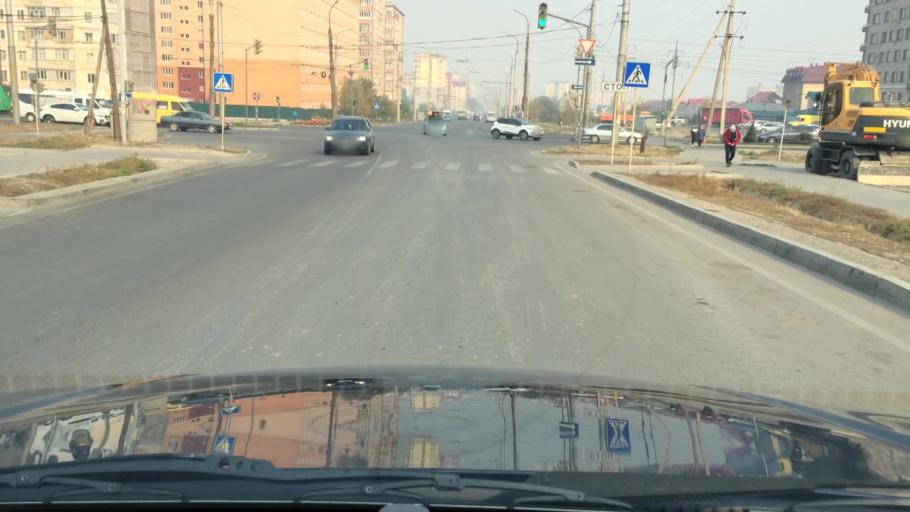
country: KG
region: Chuy
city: Bishkek
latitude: 42.8289
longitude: 74.5694
